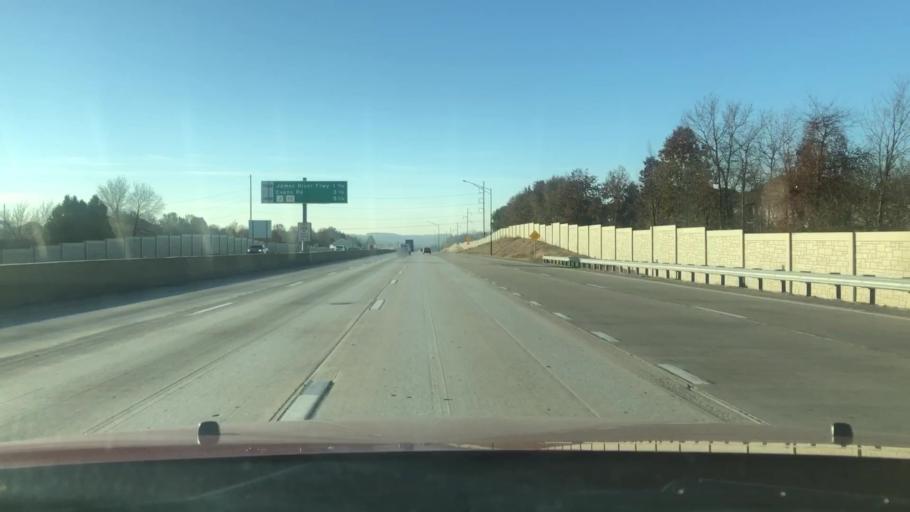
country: US
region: Missouri
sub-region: Greene County
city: Springfield
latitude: 37.1535
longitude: -93.2246
